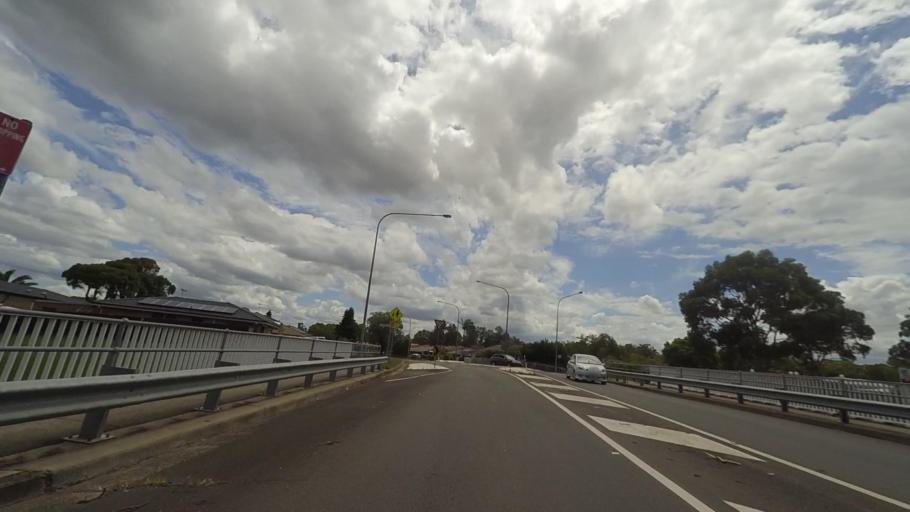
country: AU
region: New South Wales
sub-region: Fairfield
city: Fairfield Heights
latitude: -33.8675
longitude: 150.9131
